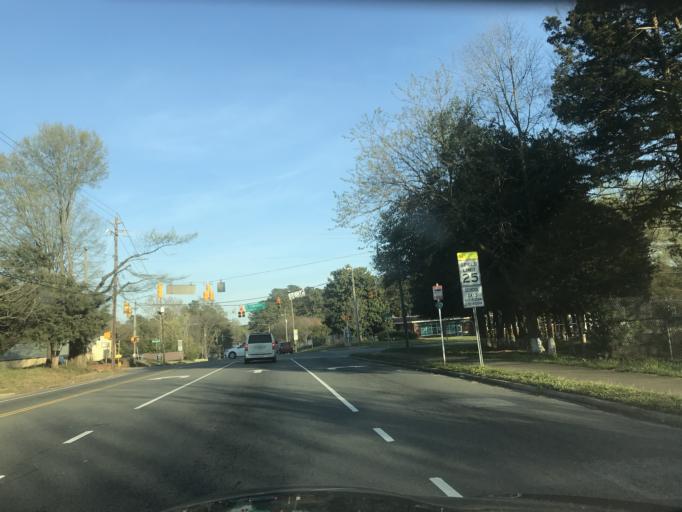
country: US
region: North Carolina
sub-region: Wake County
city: Raleigh
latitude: 35.7750
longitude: -78.6066
